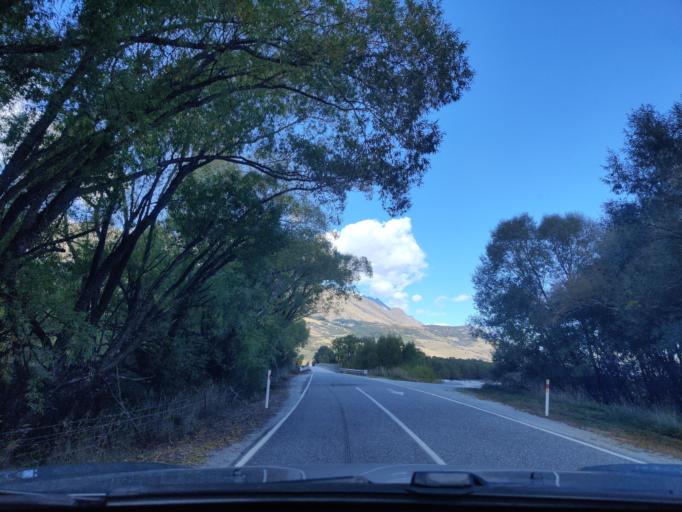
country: NZ
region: Otago
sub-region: Queenstown-Lakes District
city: Queenstown
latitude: -44.7858
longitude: 168.3955
